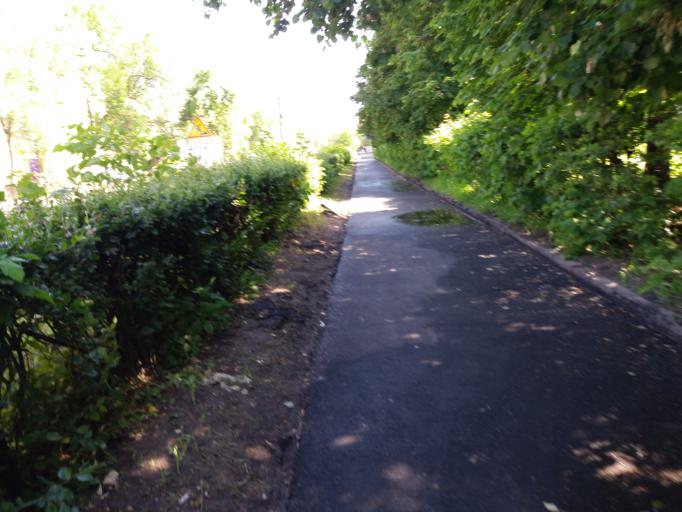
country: RU
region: Jaroslavl
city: Yaroslavl
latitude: 57.6378
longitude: 39.8499
